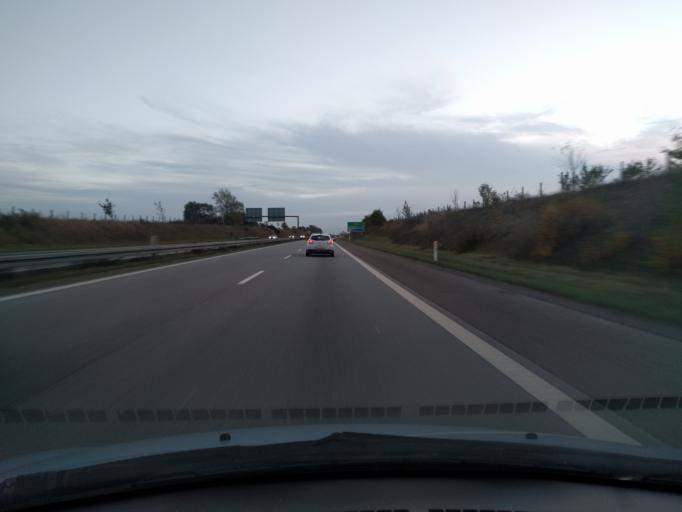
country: DK
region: South Denmark
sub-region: Odense Kommune
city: Hojby
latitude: 55.3400
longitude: 10.4530
